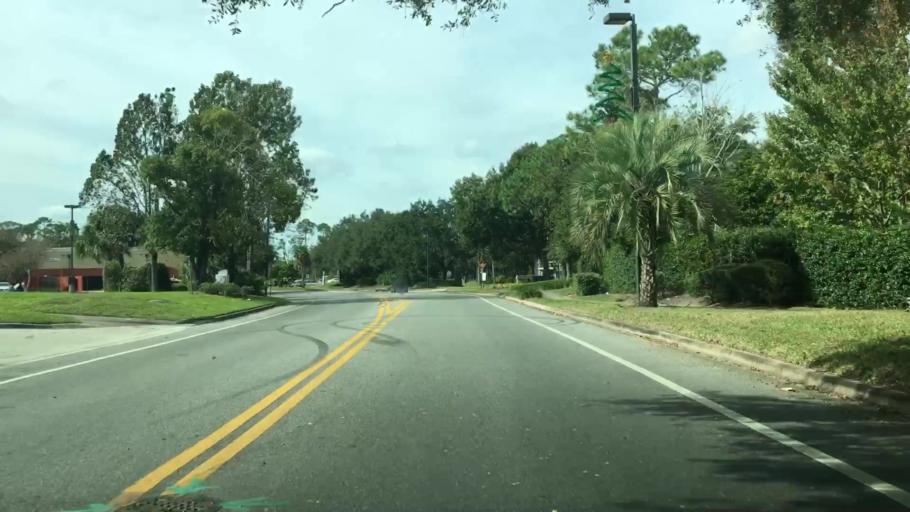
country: US
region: Florida
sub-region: Orange County
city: Conway
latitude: 28.4745
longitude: -81.3077
